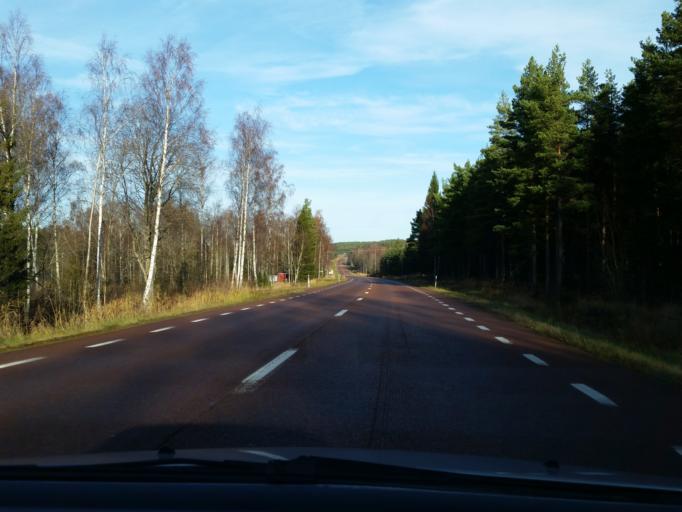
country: AX
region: Alands landsbygd
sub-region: Finstroem
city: Finstroem
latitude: 60.2924
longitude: 19.9534
